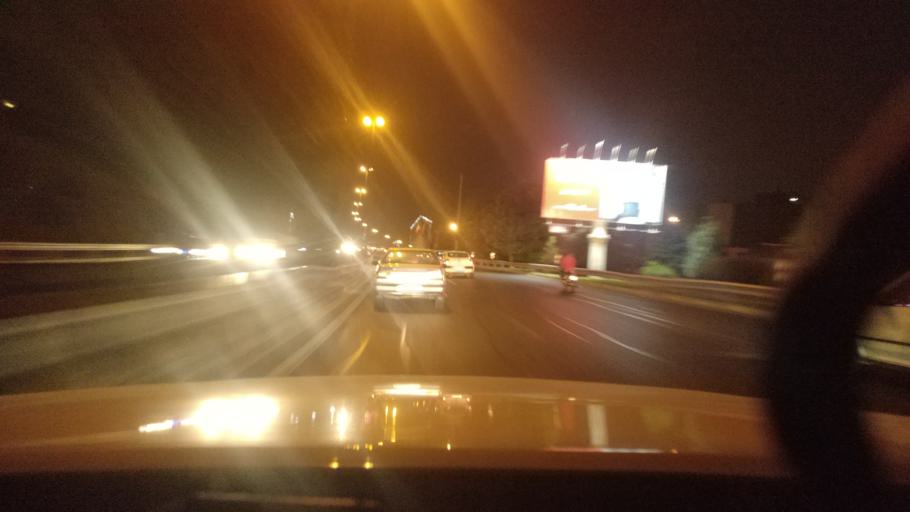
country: IR
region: Tehran
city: Tehran
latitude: 35.7361
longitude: 51.3152
